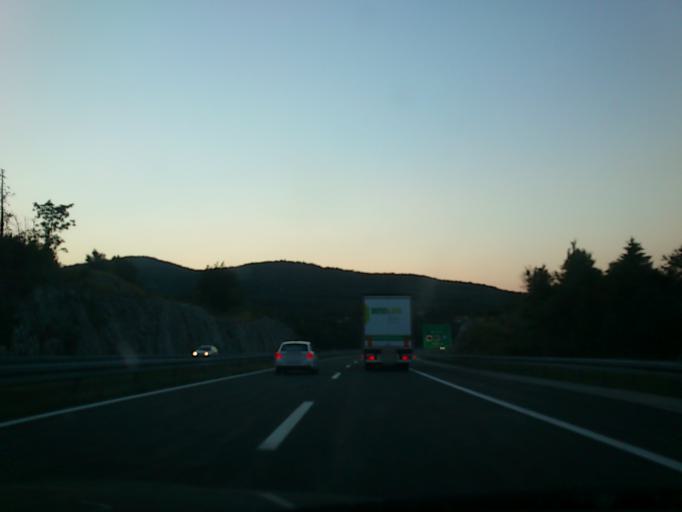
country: HR
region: Karlovacka
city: Ostarije
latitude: 45.1217
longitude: 15.2444
